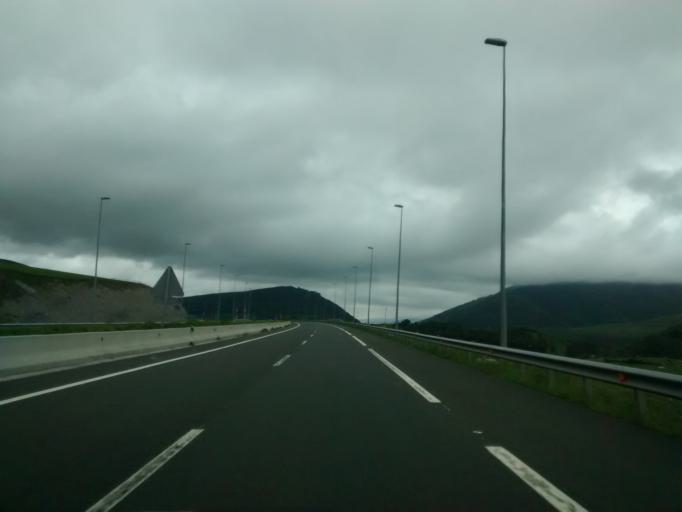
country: ES
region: Cantabria
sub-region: Provincia de Cantabria
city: Santiurde de Reinosa
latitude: 43.0666
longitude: -4.0878
